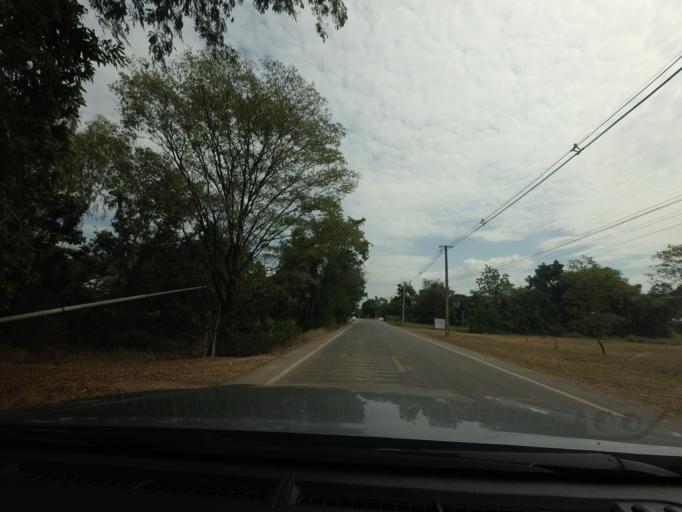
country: TH
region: Phitsanulok
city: Wang Thong
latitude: 16.7233
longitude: 100.3557
